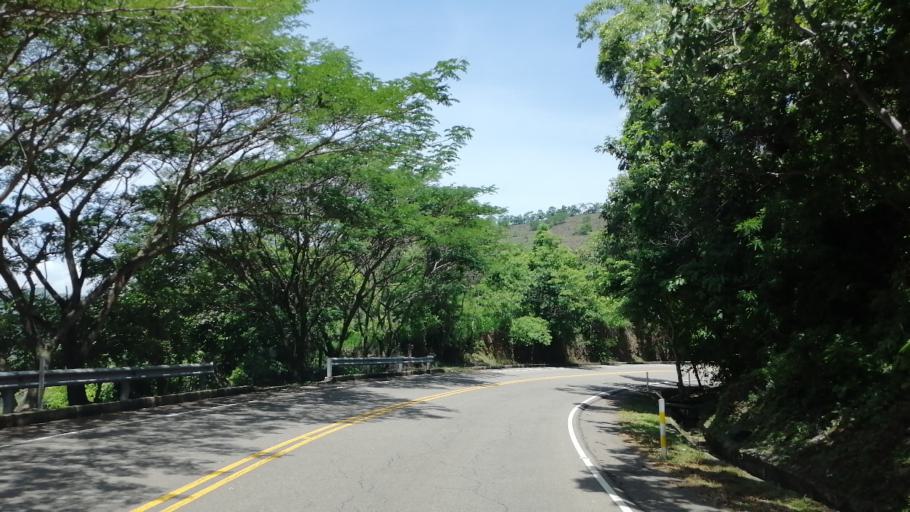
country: SV
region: Chalatenango
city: Nueva Concepcion
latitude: 14.1628
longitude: -89.3108
